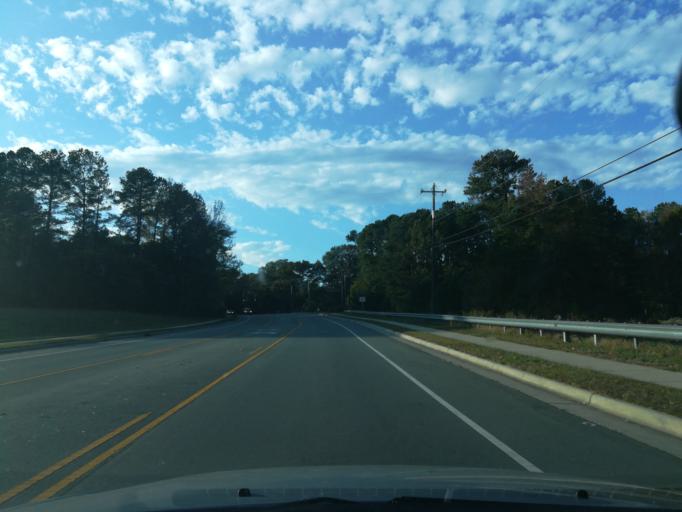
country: US
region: North Carolina
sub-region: Orange County
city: Chapel Hill
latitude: 35.9628
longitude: -79.0383
